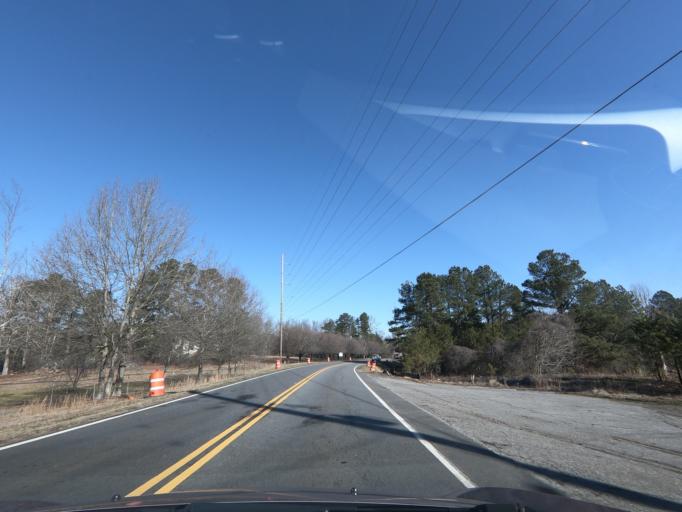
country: US
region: Georgia
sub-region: Forsyth County
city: Cumming
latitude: 34.3008
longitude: -84.1528
